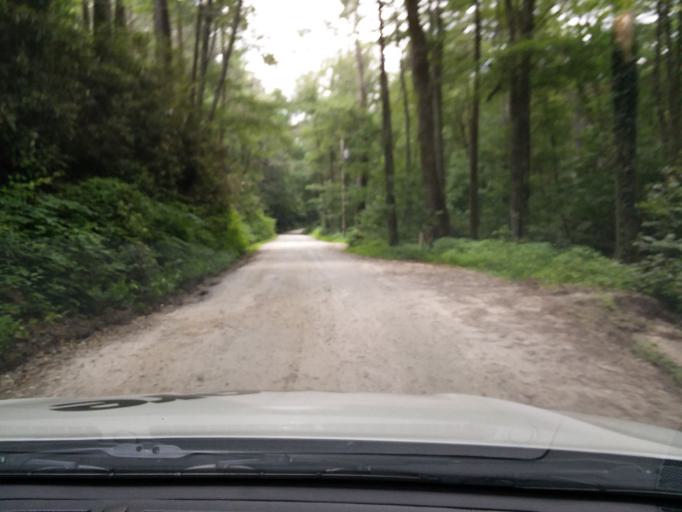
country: US
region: Georgia
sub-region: Rabun County
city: Mountain City
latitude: 35.0466
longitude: -83.2286
